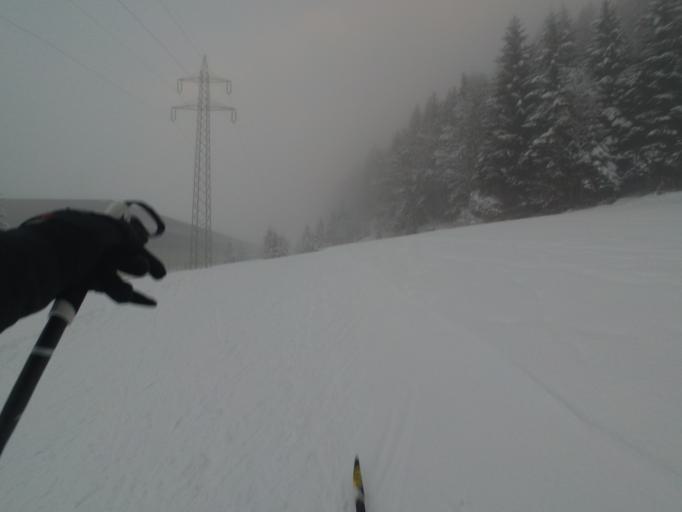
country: AT
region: Salzburg
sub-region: Politischer Bezirk Sankt Johann im Pongau
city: Wagrain
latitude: 47.3504
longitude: 13.3192
